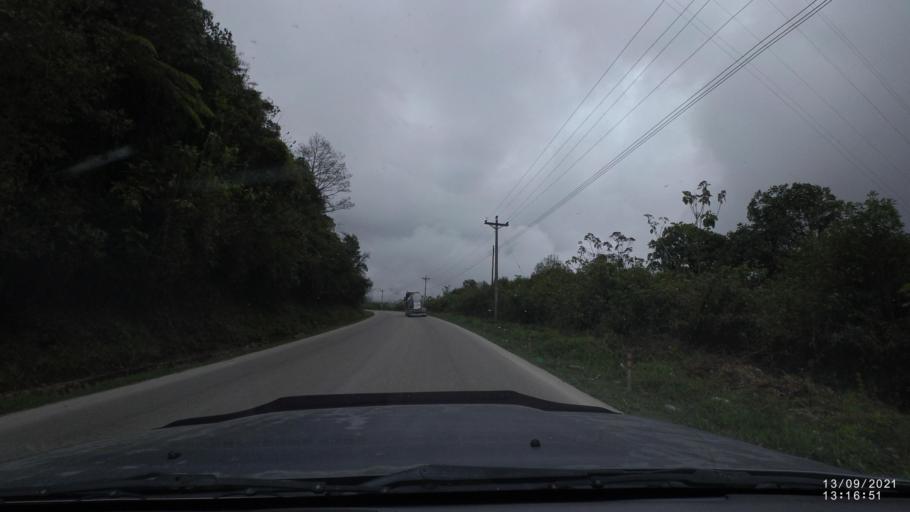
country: BO
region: Cochabamba
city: Colomi
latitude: -17.2021
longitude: -65.8602
